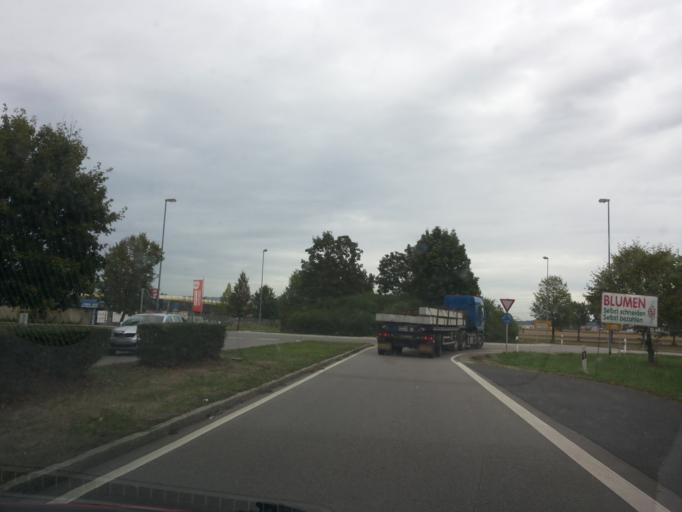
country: DE
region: Bavaria
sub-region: Upper Bavaria
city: Lenting
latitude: 48.7835
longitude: 11.4820
